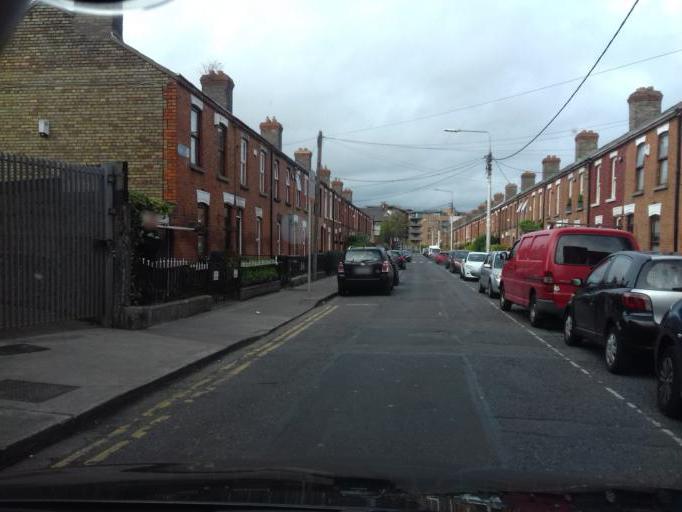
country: IE
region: Leinster
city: Rialto
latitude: 53.3346
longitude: -6.2911
